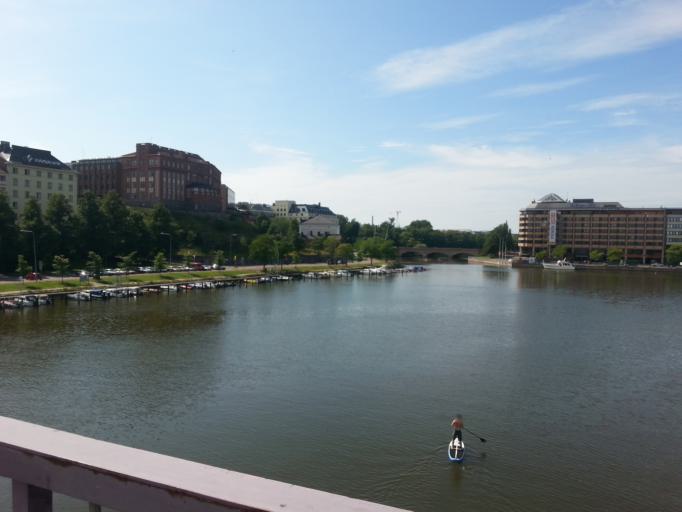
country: FI
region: Uusimaa
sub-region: Helsinki
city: Helsinki
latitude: 60.1776
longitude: 24.9572
